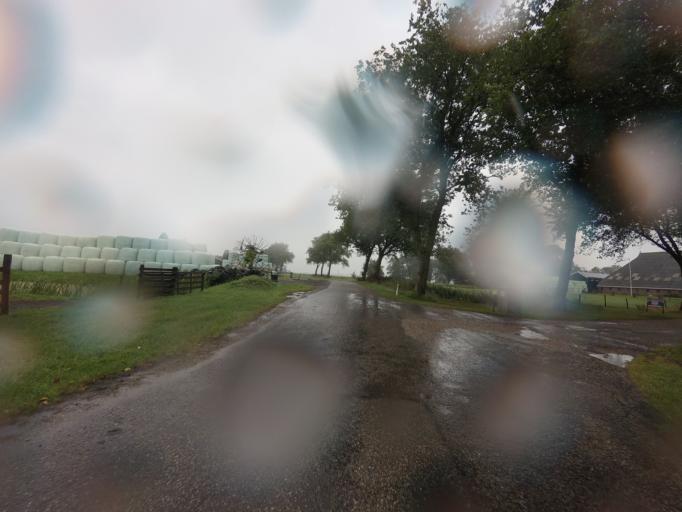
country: NL
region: Friesland
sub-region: Gemeente Boarnsterhim
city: Aldeboarn
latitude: 53.0704
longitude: 5.9286
